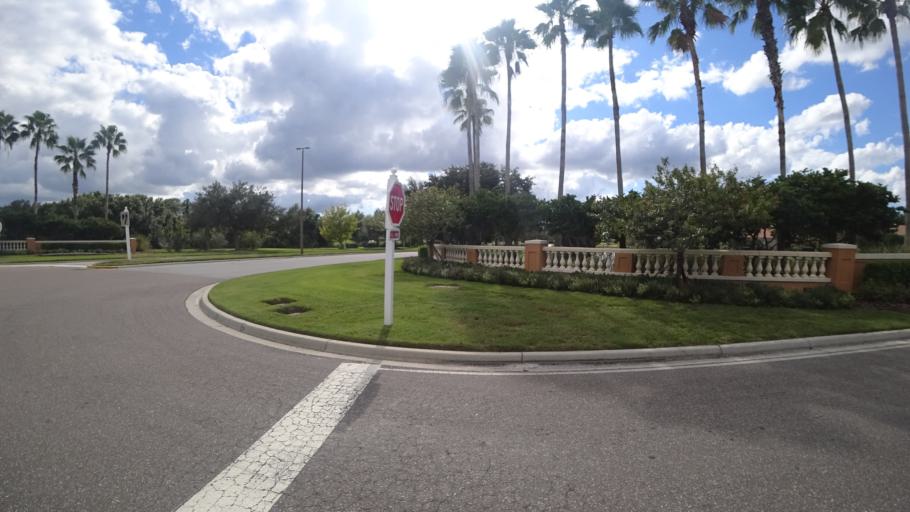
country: US
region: Florida
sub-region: Sarasota County
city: The Meadows
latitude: 27.3975
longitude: -82.4122
